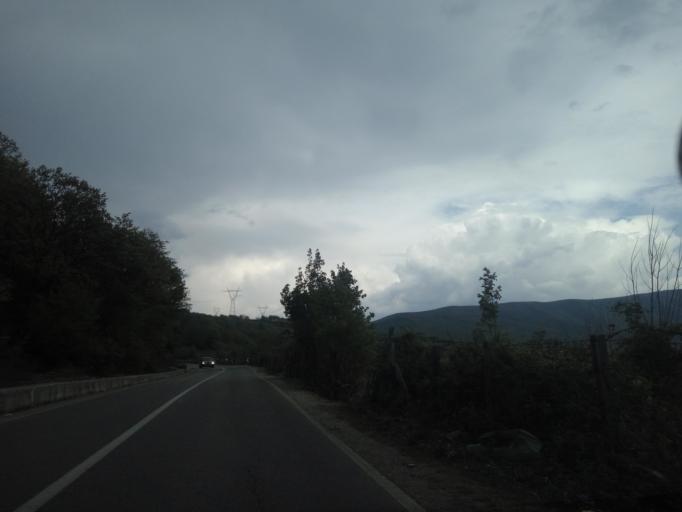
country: AL
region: Kukes
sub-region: Rrethi i Tropojes
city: Llugaj
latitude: 42.3854
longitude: 20.1590
